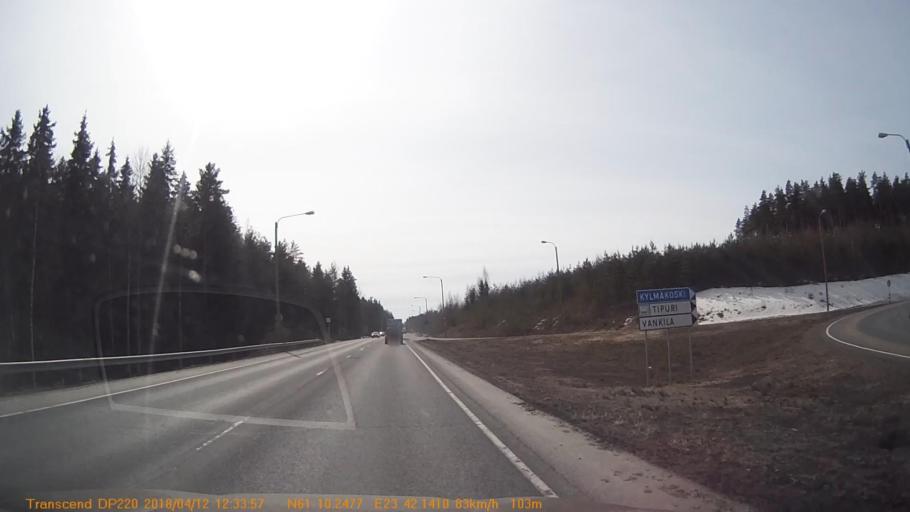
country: FI
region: Pirkanmaa
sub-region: Etelae-Pirkanmaa
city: Kylmaekoski
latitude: 61.1705
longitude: 23.7021
